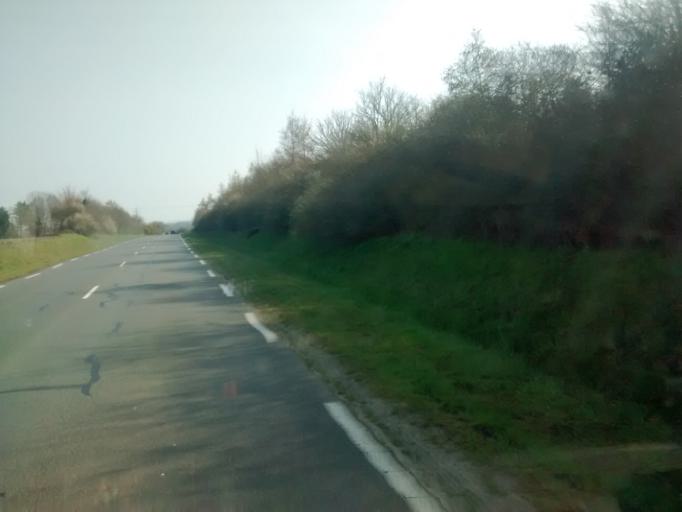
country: FR
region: Brittany
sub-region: Departement d'Ille-et-Vilaine
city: Chavagne
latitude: 48.0668
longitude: -1.7835
